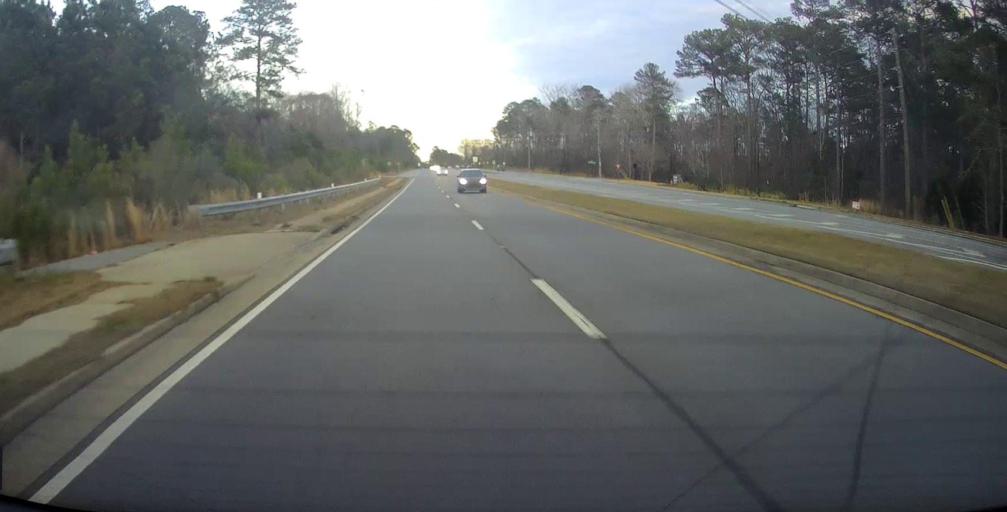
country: US
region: Alabama
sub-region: Russell County
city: Phenix City
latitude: 32.5713
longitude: -84.9254
